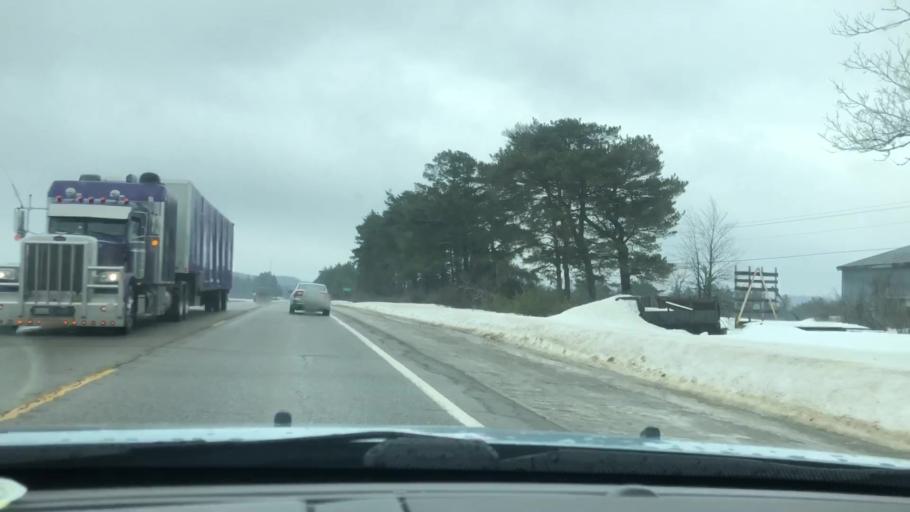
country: US
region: Michigan
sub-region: Otsego County
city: Gaylord
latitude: 45.0663
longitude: -84.8683
